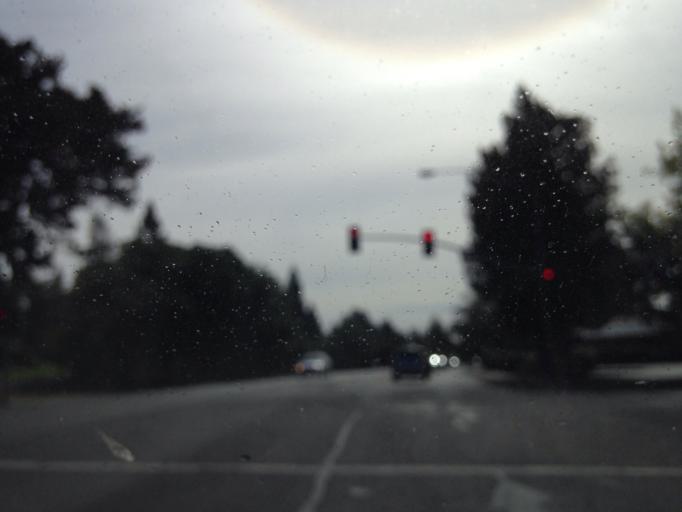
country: US
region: California
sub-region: Sonoma County
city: Sebastopol
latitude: 38.4080
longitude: -122.8390
